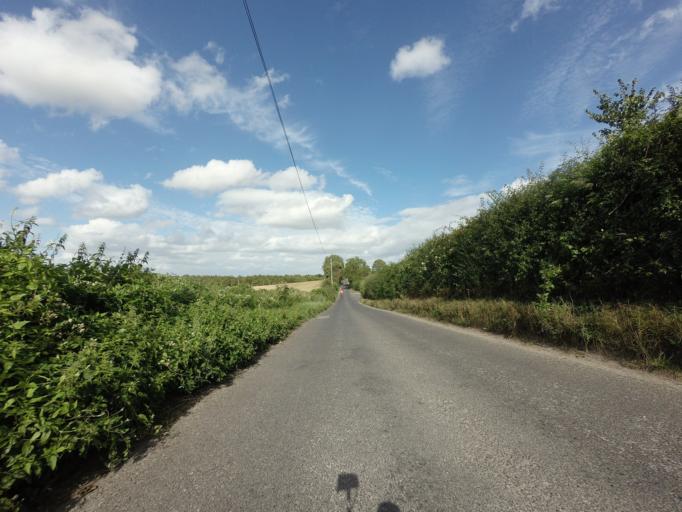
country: GB
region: England
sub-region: Kent
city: Eynsford
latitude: 51.3788
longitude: 0.2297
